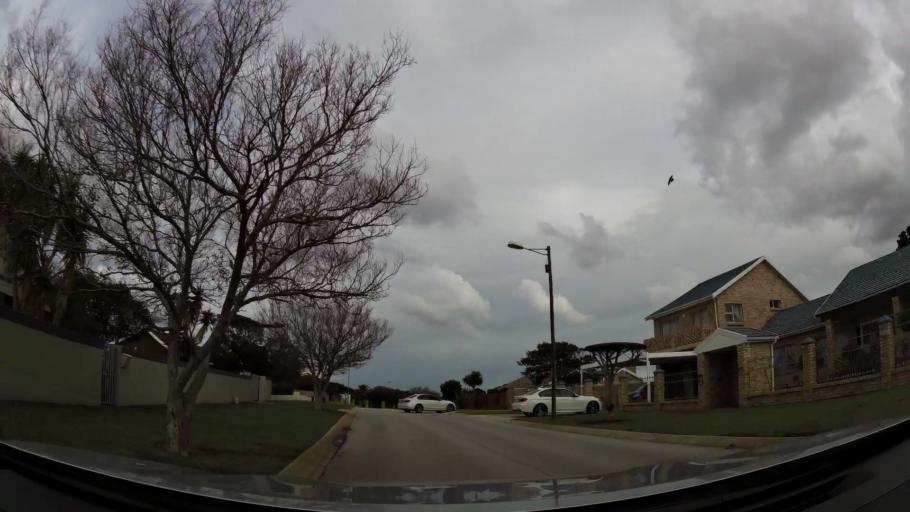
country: ZA
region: Eastern Cape
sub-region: Nelson Mandela Bay Metropolitan Municipality
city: Port Elizabeth
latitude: -33.9333
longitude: 25.5240
